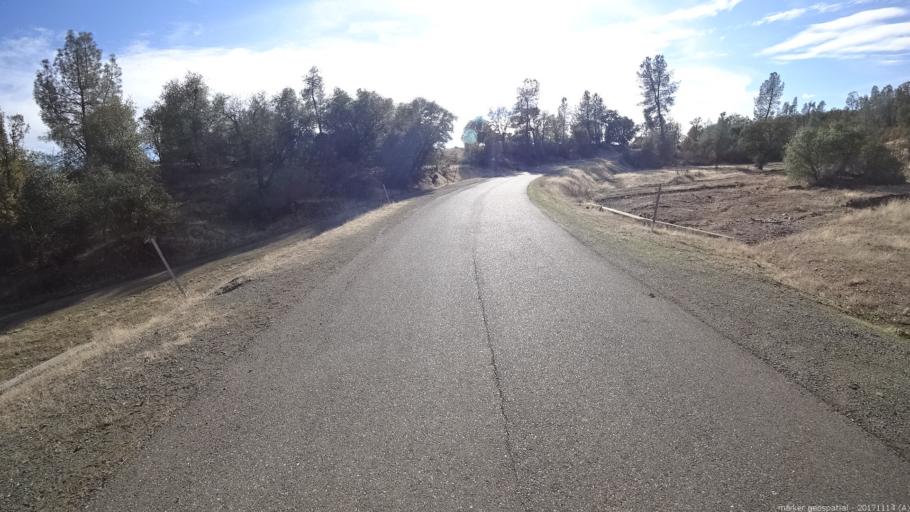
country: US
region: California
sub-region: Shasta County
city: Shasta
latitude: 40.3764
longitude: -122.5558
